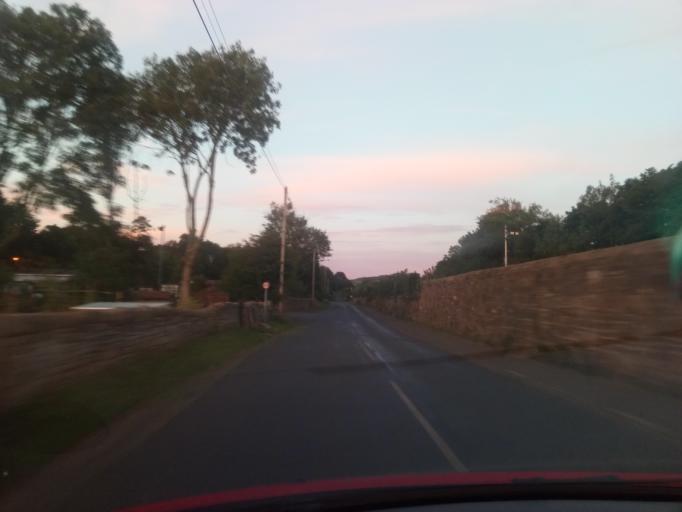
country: GB
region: England
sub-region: Northumberland
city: Bardon Mill
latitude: 54.9760
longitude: -2.2452
